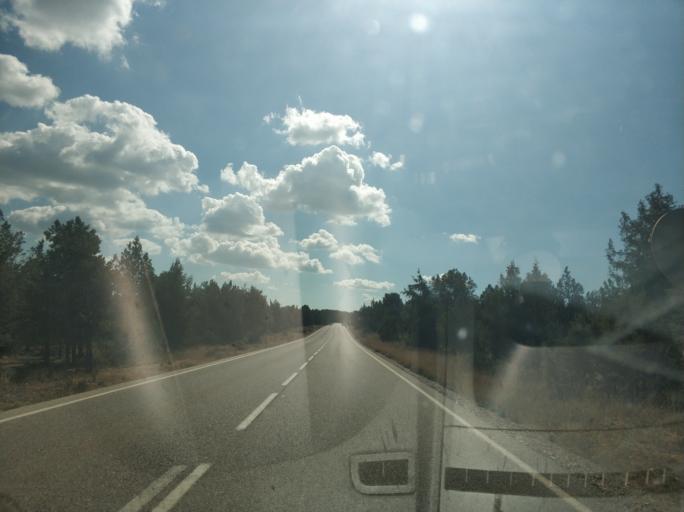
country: ES
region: Castille and Leon
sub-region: Provincia de Soria
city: Ucero
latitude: 41.7377
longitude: -3.0441
